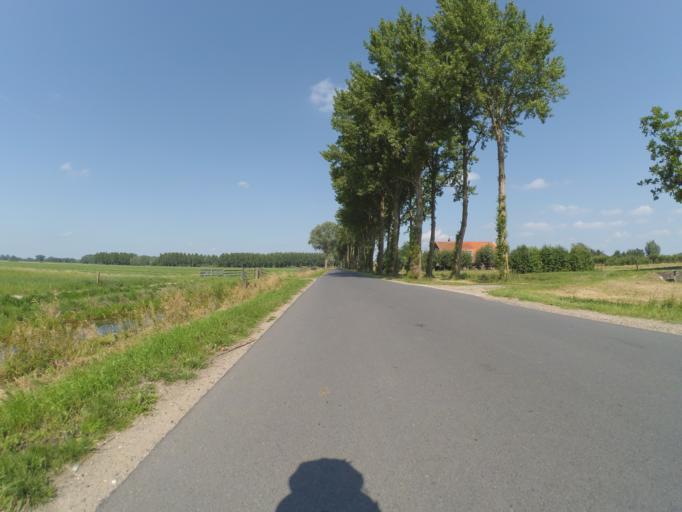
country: NL
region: South Holland
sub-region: Gemeente Leerdam
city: Leerdam
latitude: 51.9337
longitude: 5.1159
